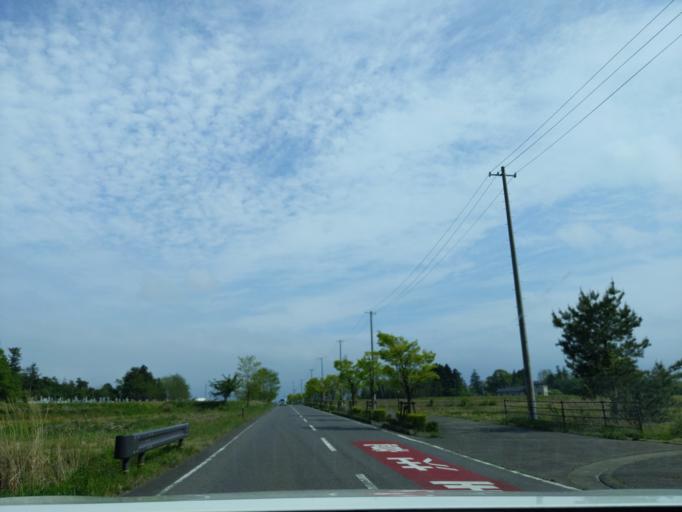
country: JP
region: Fukushima
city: Koriyama
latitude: 37.3513
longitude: 140.3297
